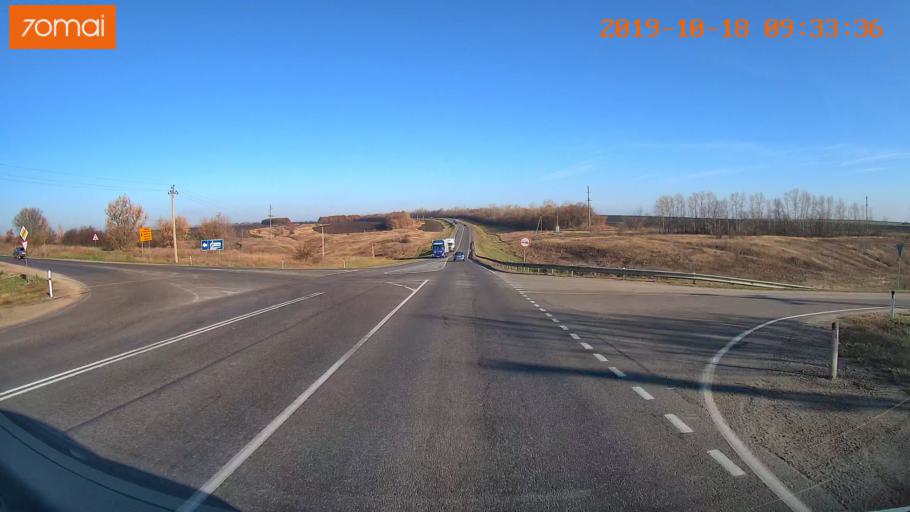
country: RU
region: Tula
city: Yefremov
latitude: 53.1689
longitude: 38.1515
